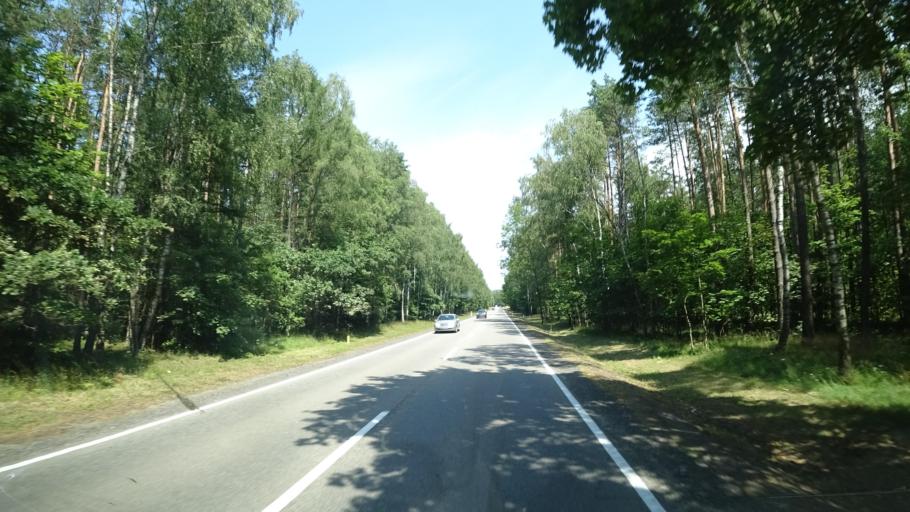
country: PL
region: Pomeranian Voivodeship
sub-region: Powiat koscierski
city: Grabowo Koscierskie
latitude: 54.1910
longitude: 18.1089
